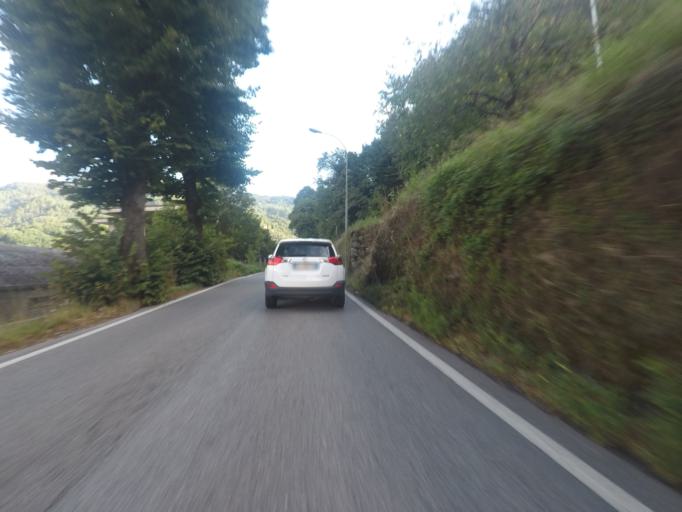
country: IT
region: Tuscany
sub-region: Provincia di Lucca
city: Bagni di Lucca
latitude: 44.0021
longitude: 10.5604
